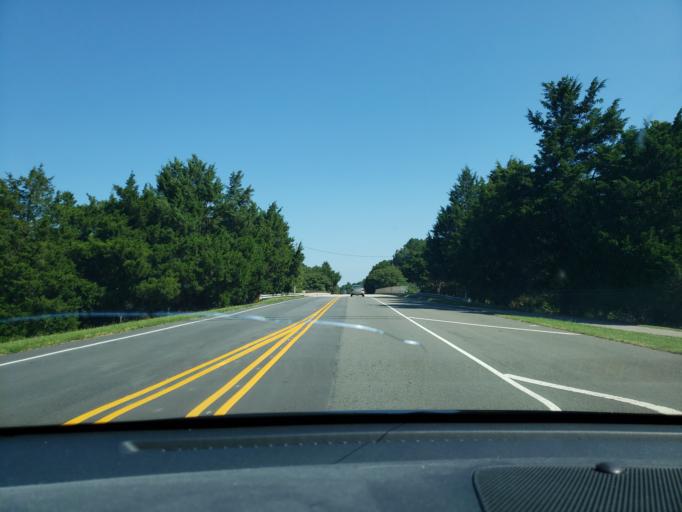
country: US
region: North Carolina
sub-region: Durham County
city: Durham
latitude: 35.9016
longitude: -78.8797
